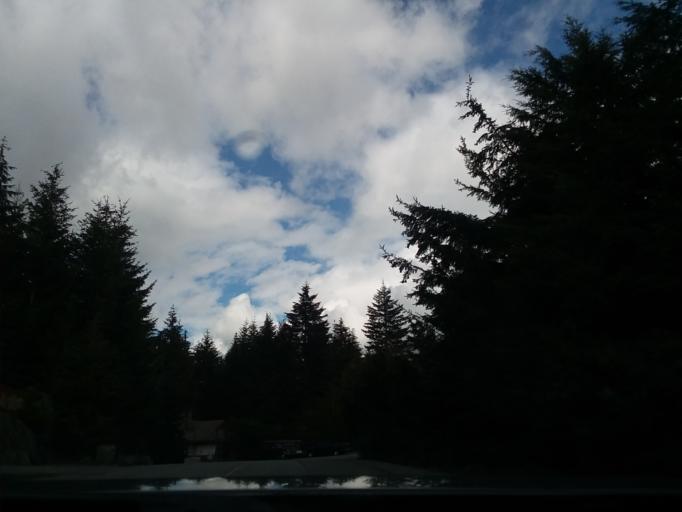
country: CA
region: British Columbia
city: Whistler
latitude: 50.1030
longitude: -122.9852
